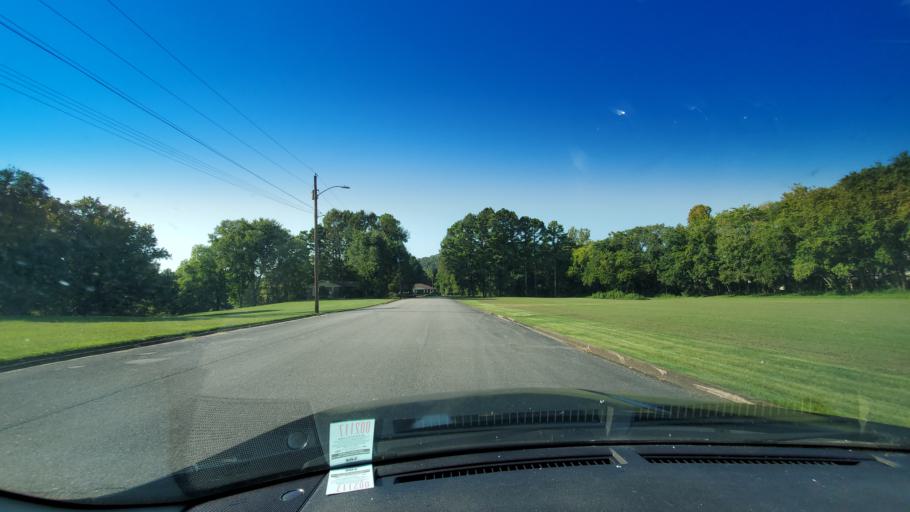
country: US
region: Tennessee
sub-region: Smith County
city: Carthage
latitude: 36.2608
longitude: -85.9585
